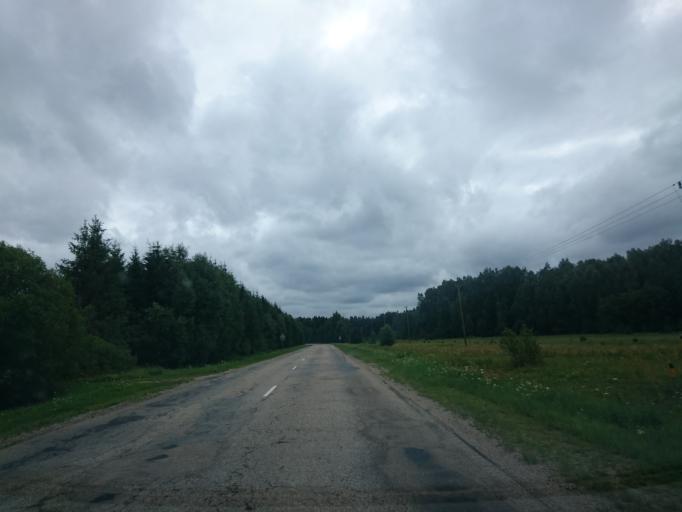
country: LV
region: Pavilostas
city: Pavilosta
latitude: 56.8112
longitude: 21.2259
